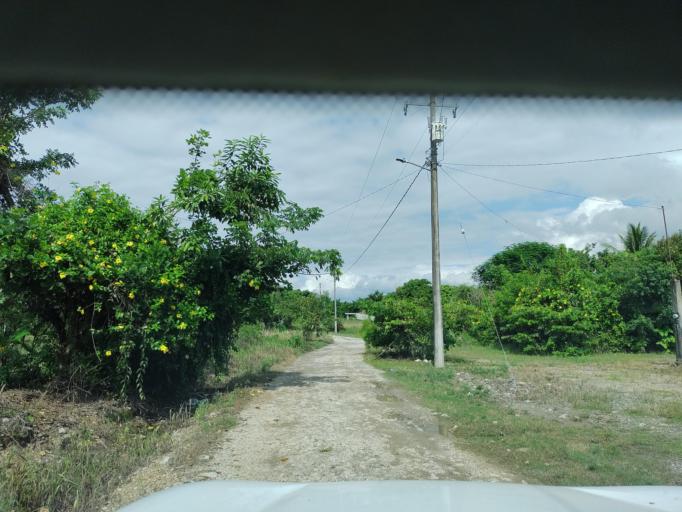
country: MX
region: Veracruz
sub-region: Atzalan
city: Colonias Pedernales
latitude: 20.0418
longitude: -97.0764
